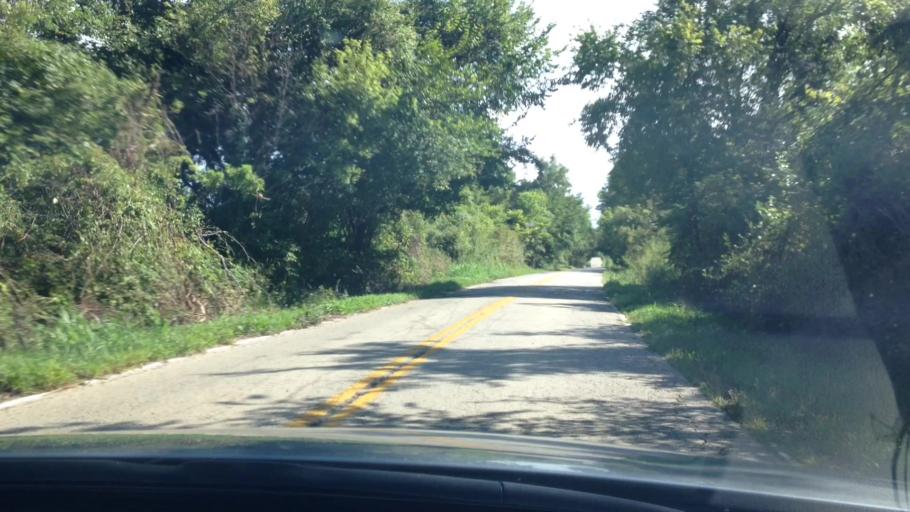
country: US
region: Missouri
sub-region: Platte County
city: Weatherby Lake
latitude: 39.3212
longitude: -94.6664
